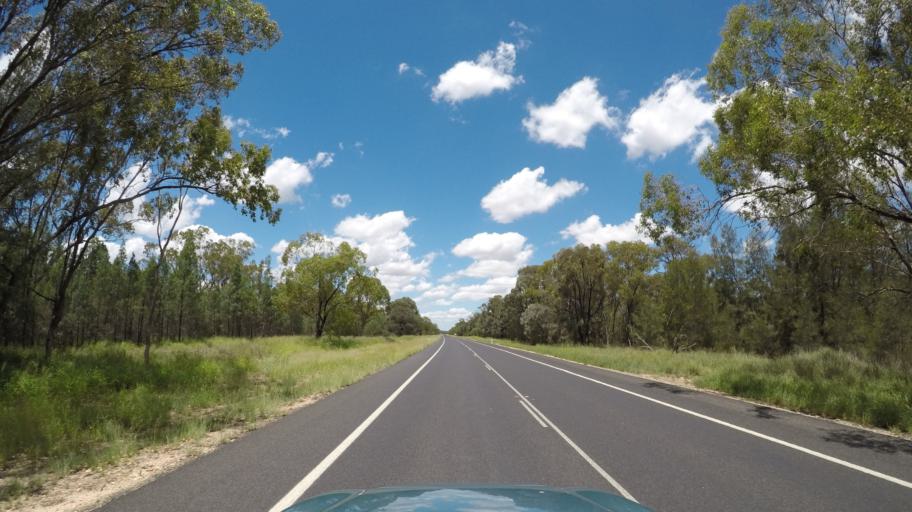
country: AU
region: Queensland
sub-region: Goondiwindi
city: Goondiwindi
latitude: -28.0937
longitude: 150.7279
